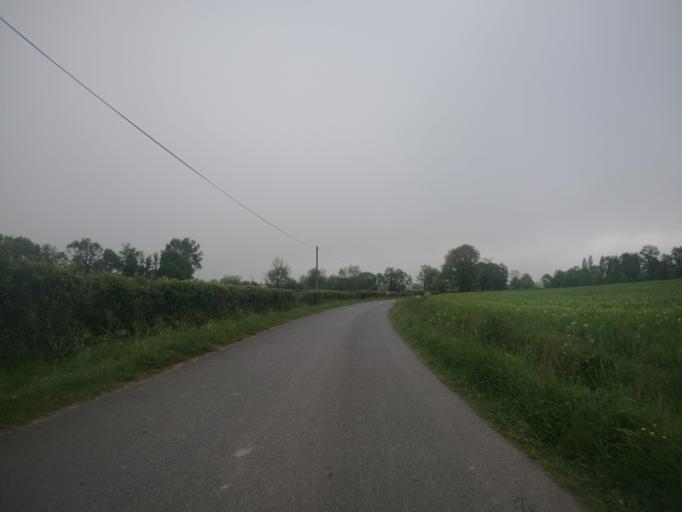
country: FR
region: Poitou-Charentes
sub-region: Departement des Deux-Sevres
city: Chiche
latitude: 46.8732
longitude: -0.3358
